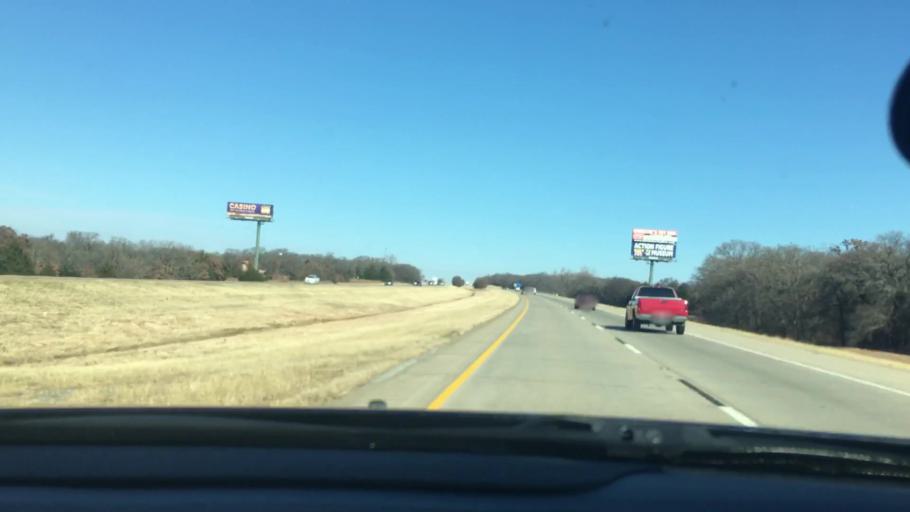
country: US
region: Oklahoma
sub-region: Love County
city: Marietta
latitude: 34.0522
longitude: -97.1486
